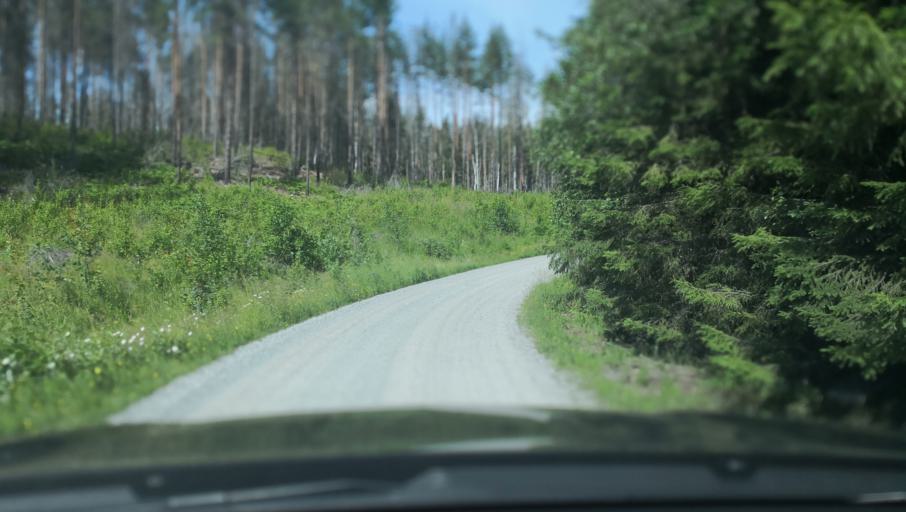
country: SE
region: Vaestmanland
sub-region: Surahammars Kommun
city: Ramnas
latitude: 59.8919
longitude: 16.0998
